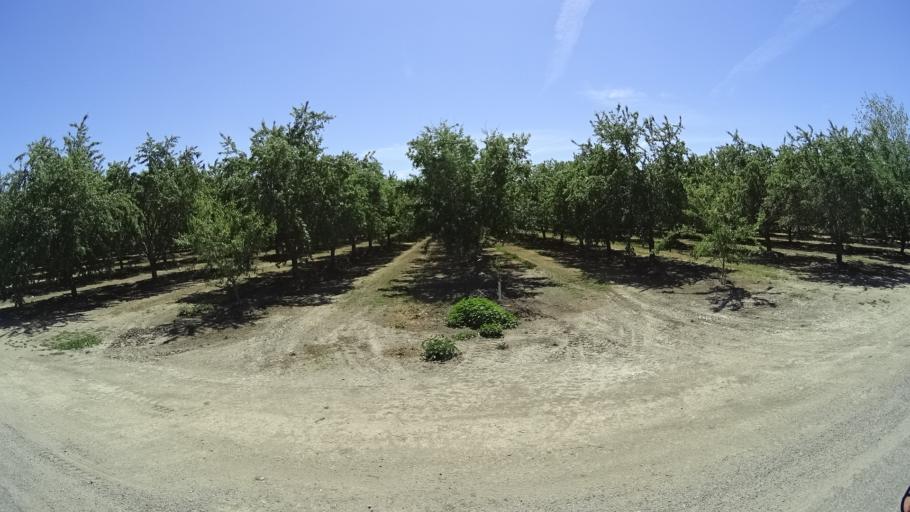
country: US
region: California
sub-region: Glenn County
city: Hamilton City
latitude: 39.7214
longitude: -122.0920
